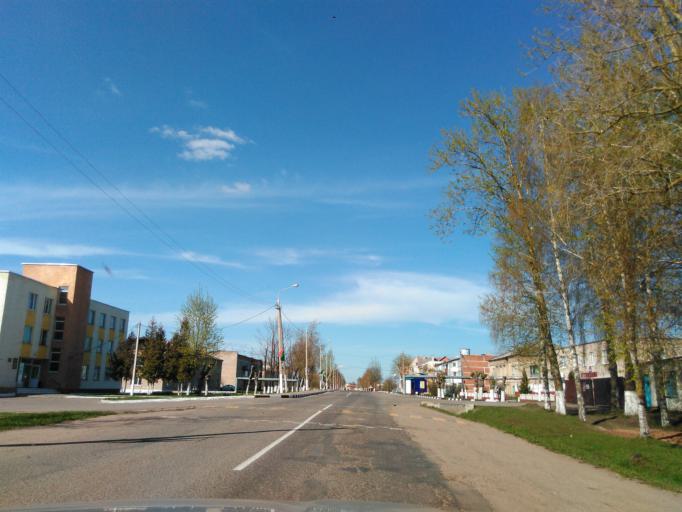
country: BY
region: Vitebsk
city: Chashniki
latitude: 54.8517
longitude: 29.1563
